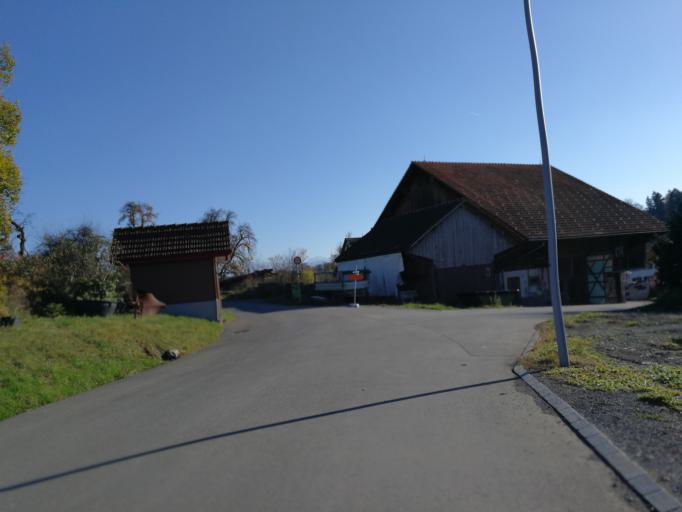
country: CH
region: Zurich
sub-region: Bezirk Meilen
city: Oetwil am See
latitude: 47.2754
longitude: 8.7321
